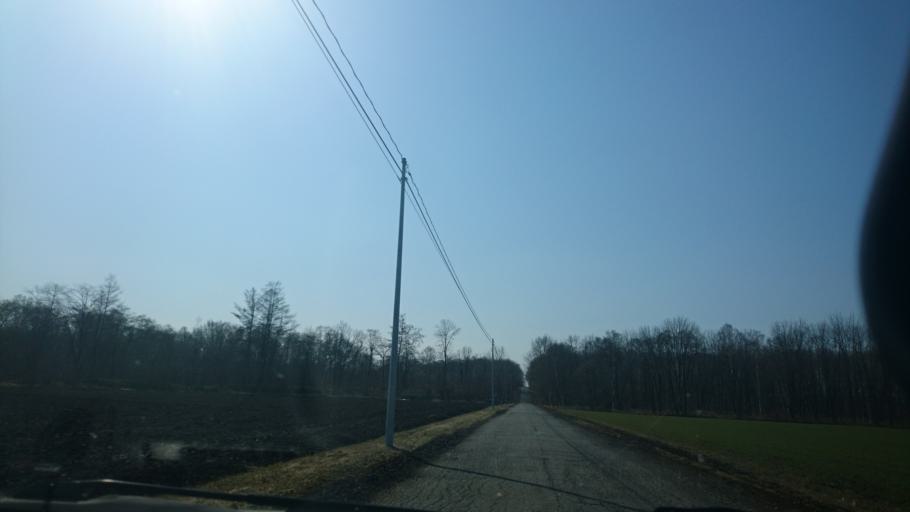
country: JP
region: Hokkaido
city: Obihiro
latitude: 42.9181
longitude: 143.0898
